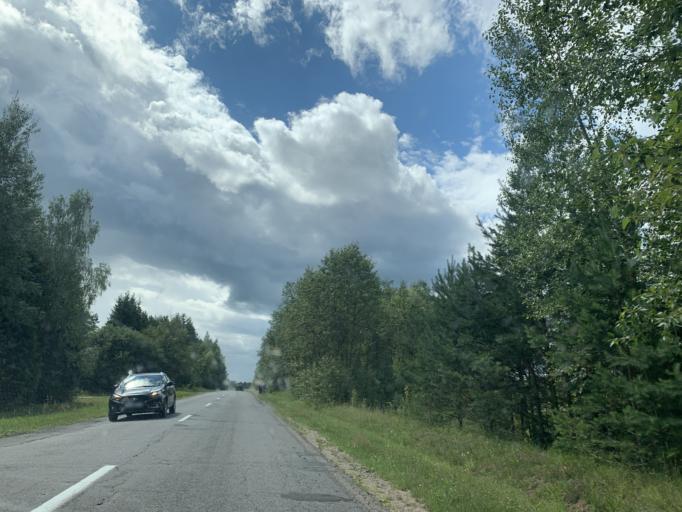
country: BY
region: Minsk
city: Ivyanyets
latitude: 53.9735
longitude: 26.8602
